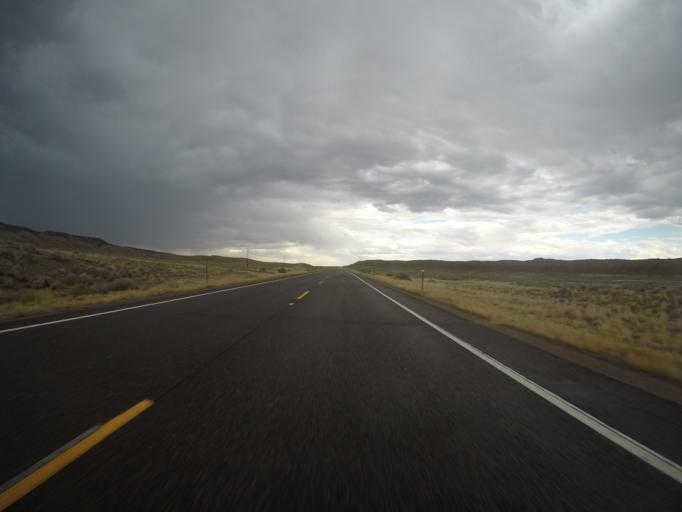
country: US
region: Colorado
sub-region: Rio Blanco County
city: Rangely
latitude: 40.2515
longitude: -108.8478
